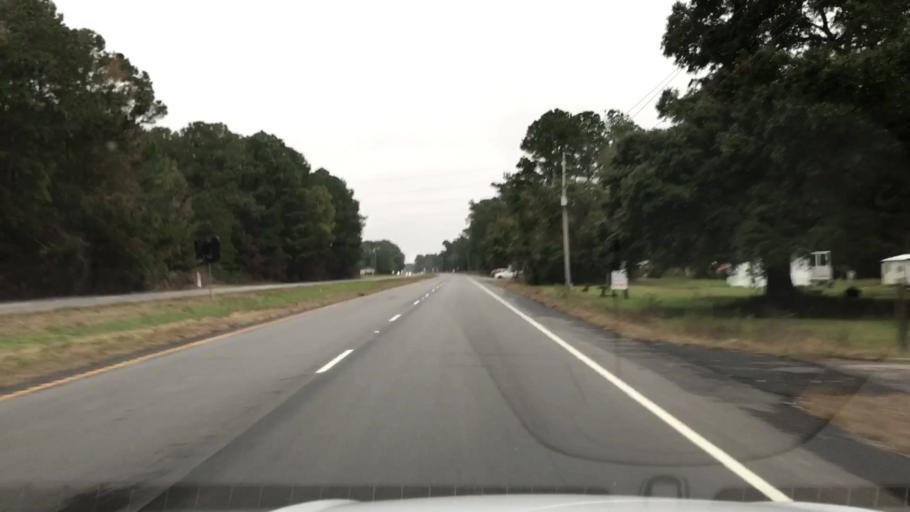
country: US
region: South Carolina
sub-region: Charleston County
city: Awendaw
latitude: 33.0877
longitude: -79.4884
